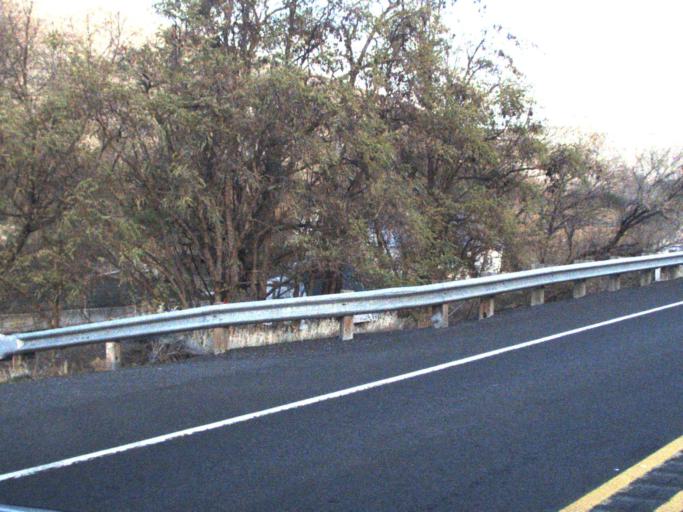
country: US
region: Washington
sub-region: Garfield County
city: Pomeroy
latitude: 46.6638
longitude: -117.7981
